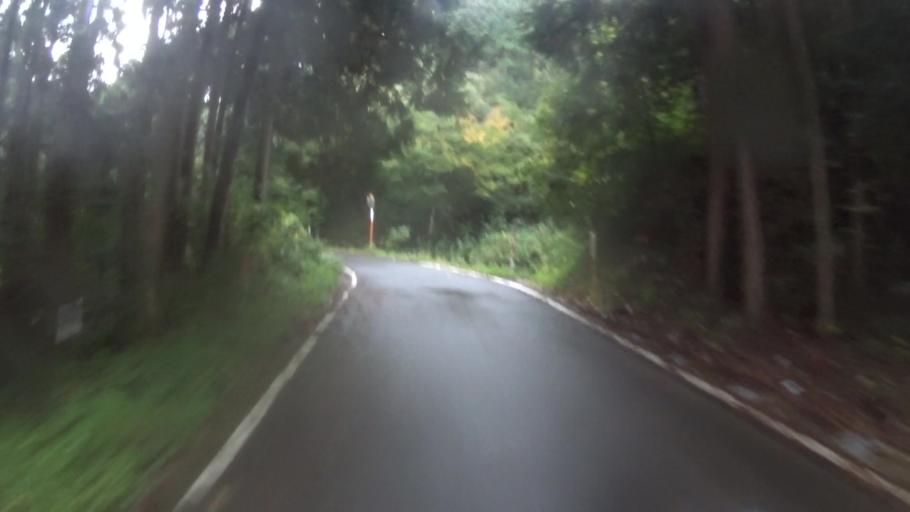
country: JP
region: Kyoto
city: Miyazu
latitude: 35.5267
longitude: 135.2324
